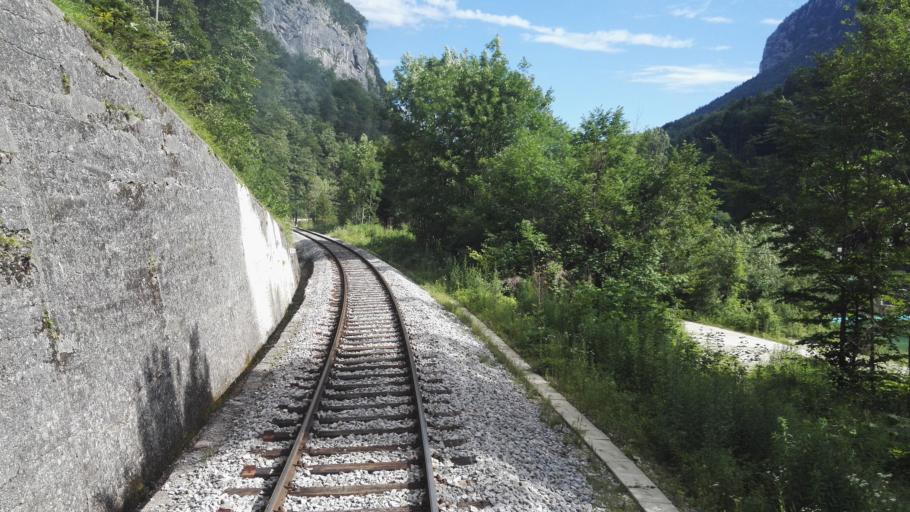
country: SI
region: Gorje
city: Zgornje Gorje
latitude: 46.3110
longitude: 14.0621
